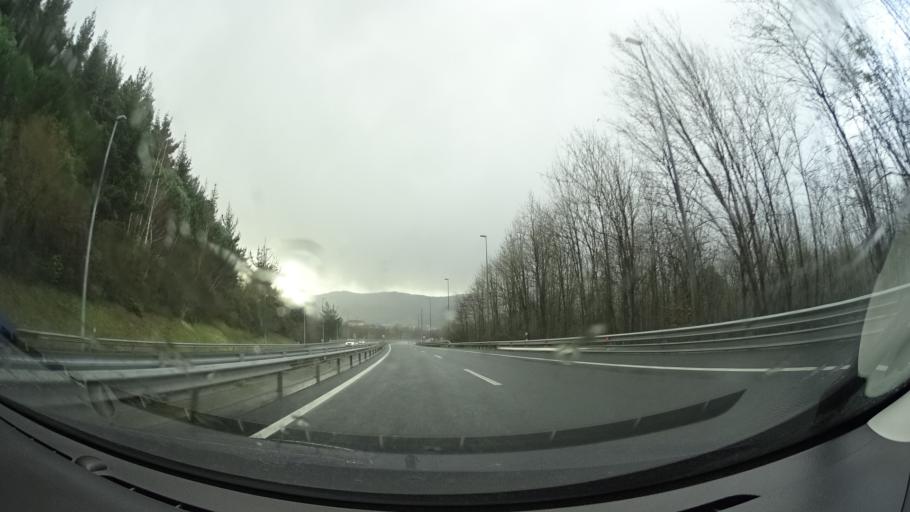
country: ES
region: Basque Country
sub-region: Bizkaia
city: Derio
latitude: 43.3087
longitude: -2.8802
